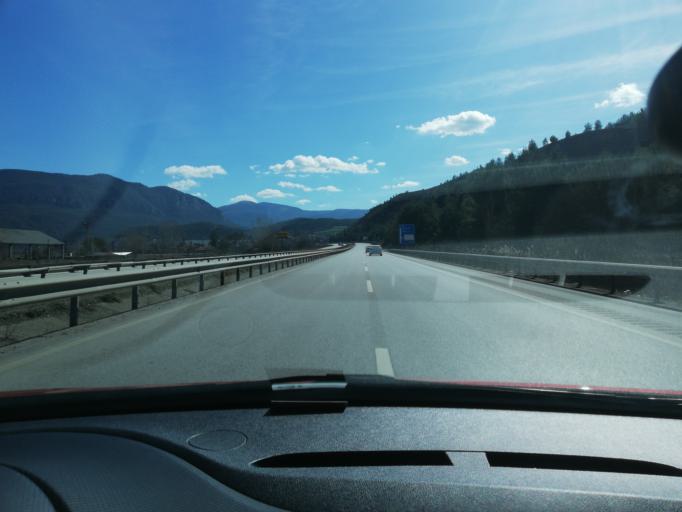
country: TR
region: Karabuk
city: Karabuk
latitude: 41.1418
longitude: 32.6671
